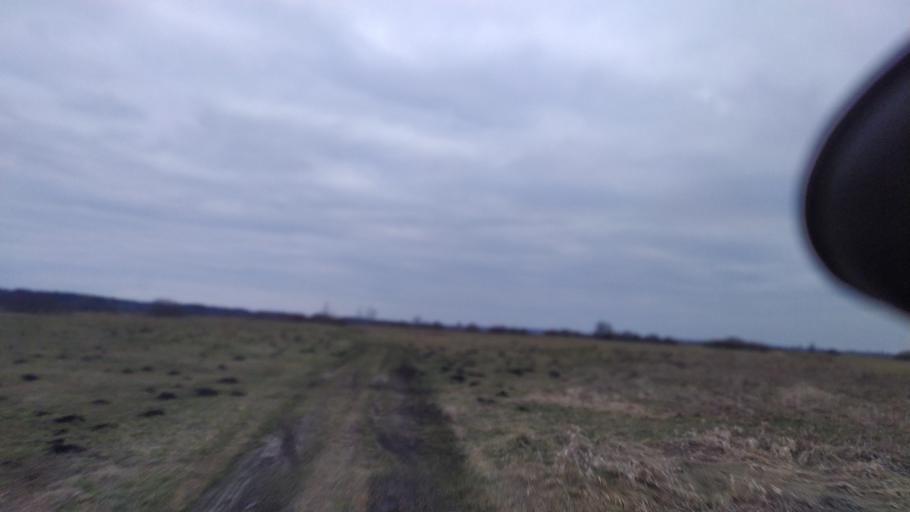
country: PL
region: Lublin Voivodeship
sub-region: Powiat lubartowski
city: Abramow
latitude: 51.4307
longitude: 22.3231
